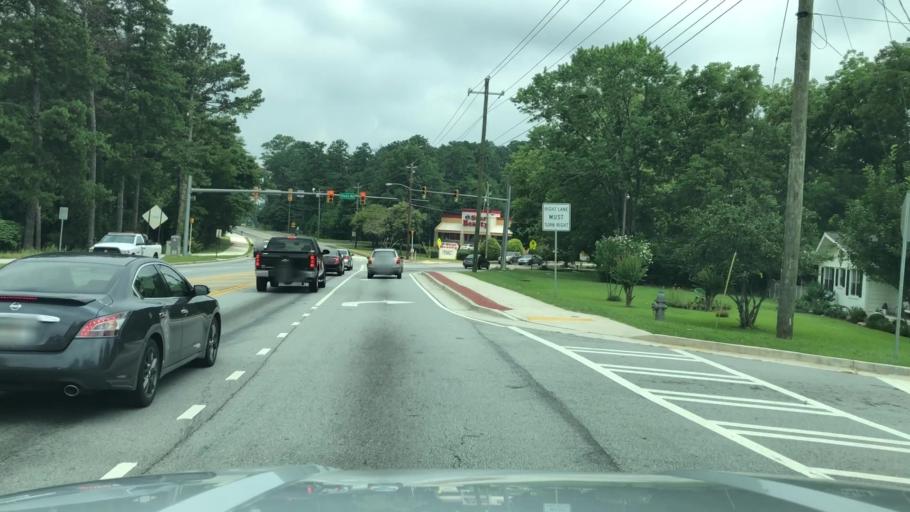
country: US
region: Georgia
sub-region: Cobb County
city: Mableton
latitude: 33.8400
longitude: -84.5776
